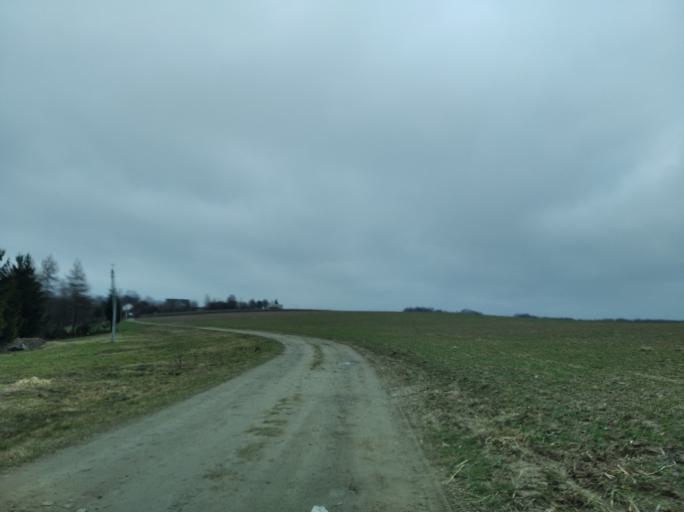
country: PL
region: Subcarpathian Voivodeship
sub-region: Powiat strzyzowski
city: Strzyzow
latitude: 49.8852
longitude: 21.7990
